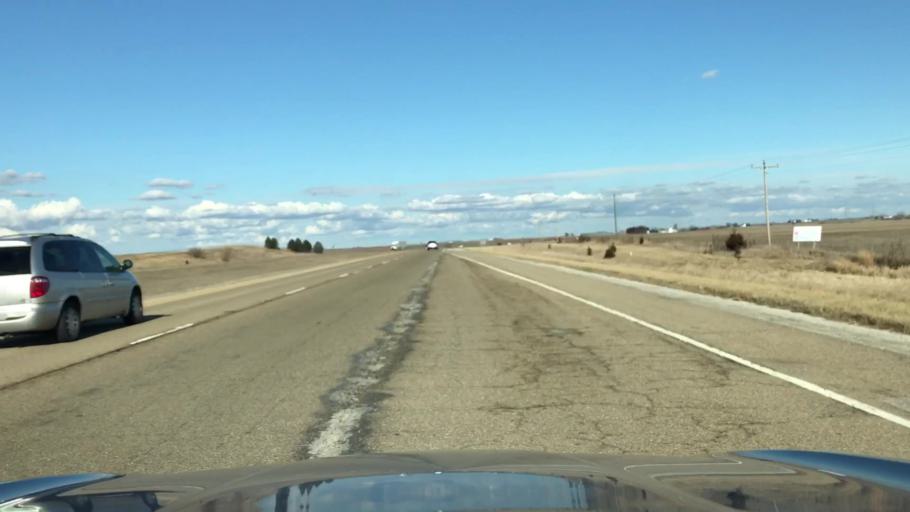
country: US
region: Illinois
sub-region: McLean County
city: Lexington
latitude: 40.6494
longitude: -88.8068
